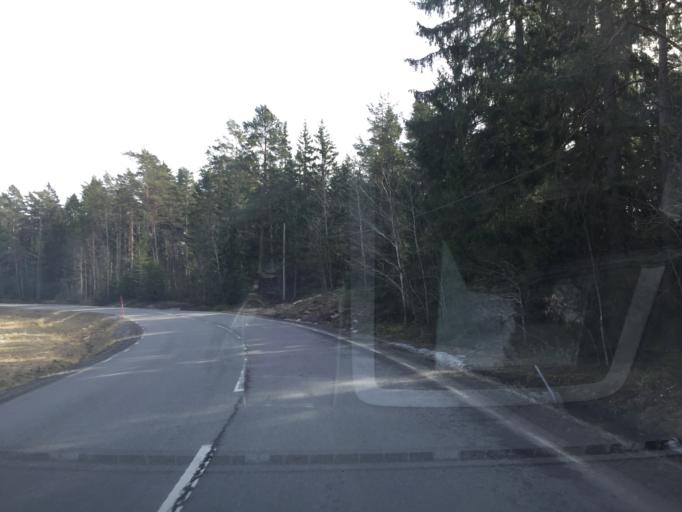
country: SE
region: Stockholm
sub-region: Huddinge Kommun
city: Huddinge
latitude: 59.1283
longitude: 17.9982
